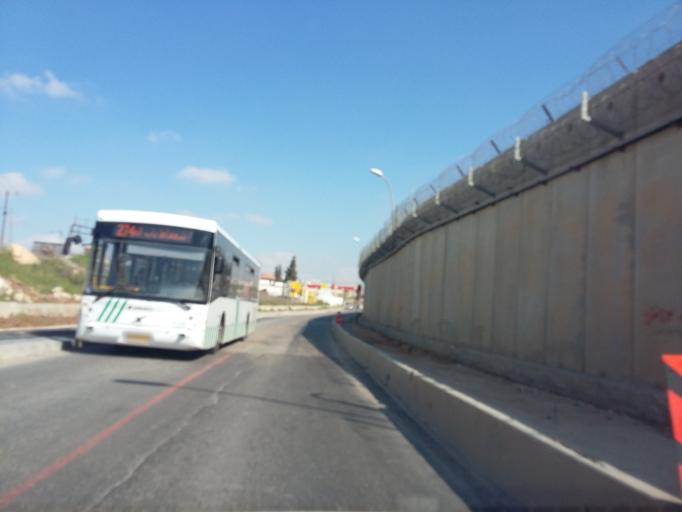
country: PS
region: West Bank
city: Ar Ram wa Dahiyat al Barid
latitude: 31.8533
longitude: 35.2246
